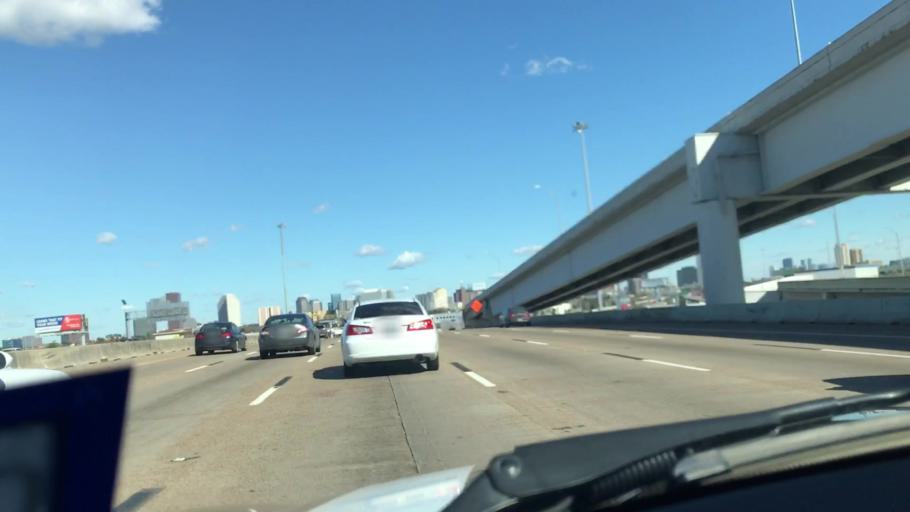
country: US
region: Texas
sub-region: Harris County
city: Bellaire
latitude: 29.7233
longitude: -95.4916
